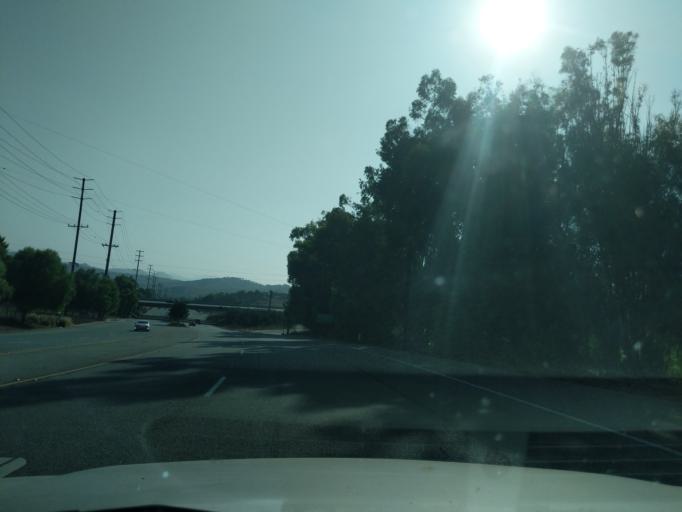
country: US
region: California
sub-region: Ventura County
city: Moorpark
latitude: 34.2684
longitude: -118.8488
